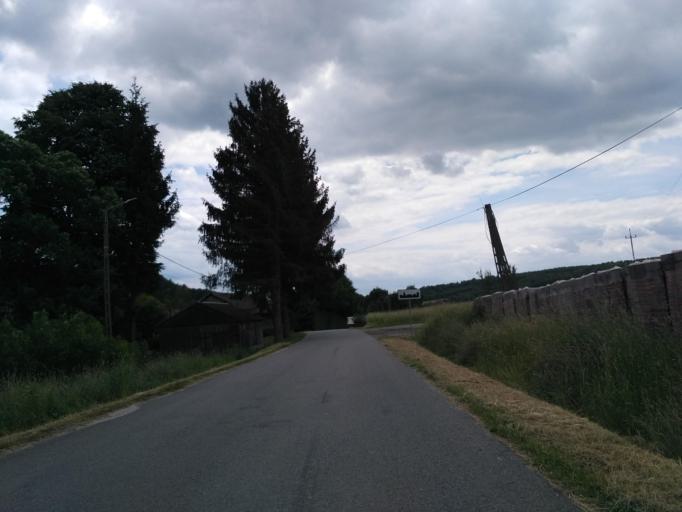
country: PL
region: Subcarpathian Voivodeship
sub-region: Powiat przeworski
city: Jawornik Polski
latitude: 49.8590
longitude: 22.2872
